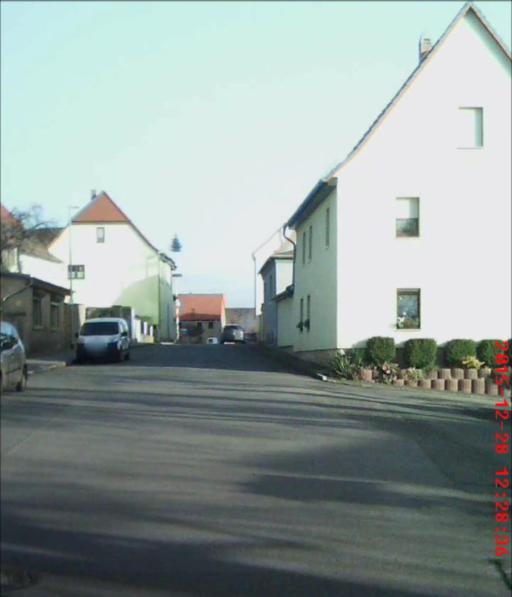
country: DE
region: Thuringia
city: Ossmanstedt
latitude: 51.0179
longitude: 11.4288
